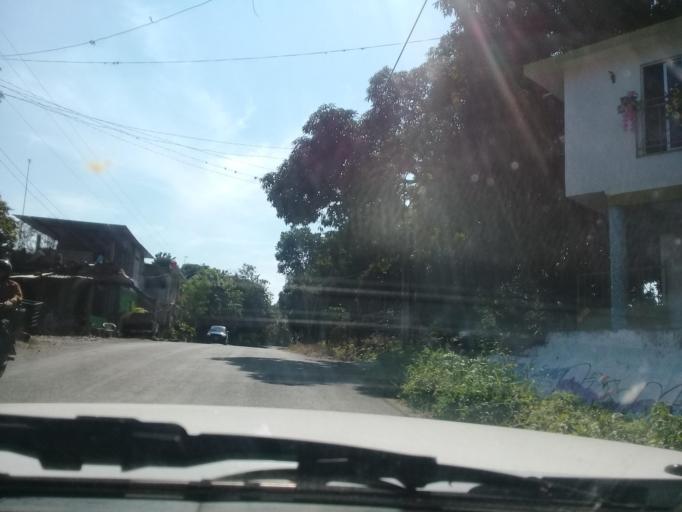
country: MX
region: Veracruz
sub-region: Emiliano Zapata
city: Plan del Rio
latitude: 19.4235
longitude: -96.6139
